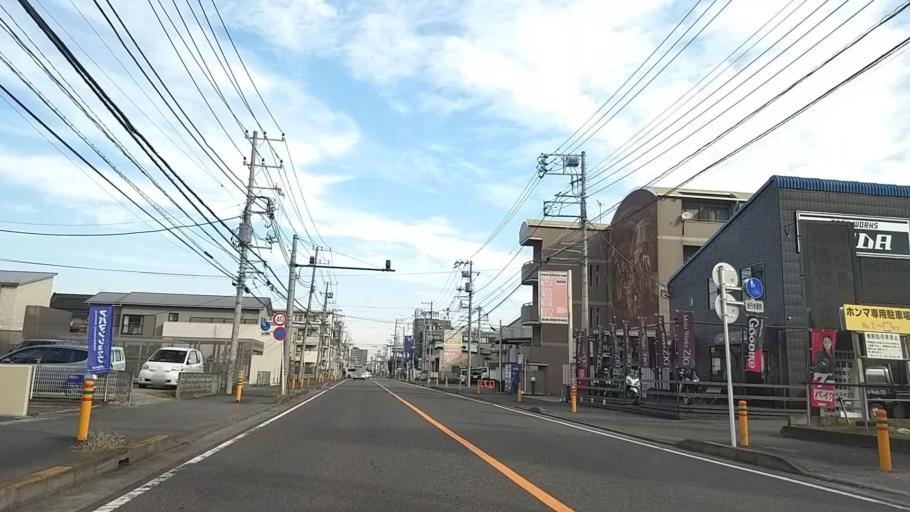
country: JP
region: Kanagawa
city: Atsugi
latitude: 35.4250
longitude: 139.3654
